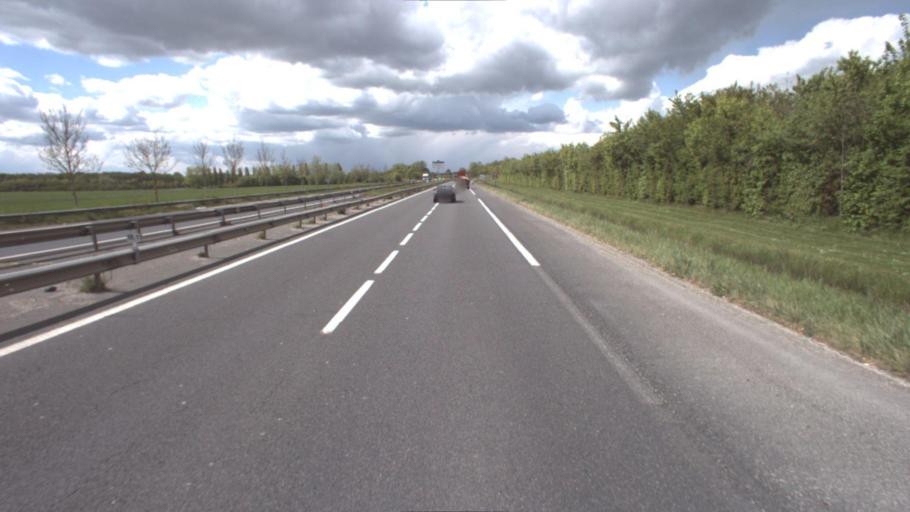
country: FR
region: Ile-de-France
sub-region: Departement de Seine-et-Marne
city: Neufmoutiers-en-Brie
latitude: 48.7263
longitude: 2.8200
